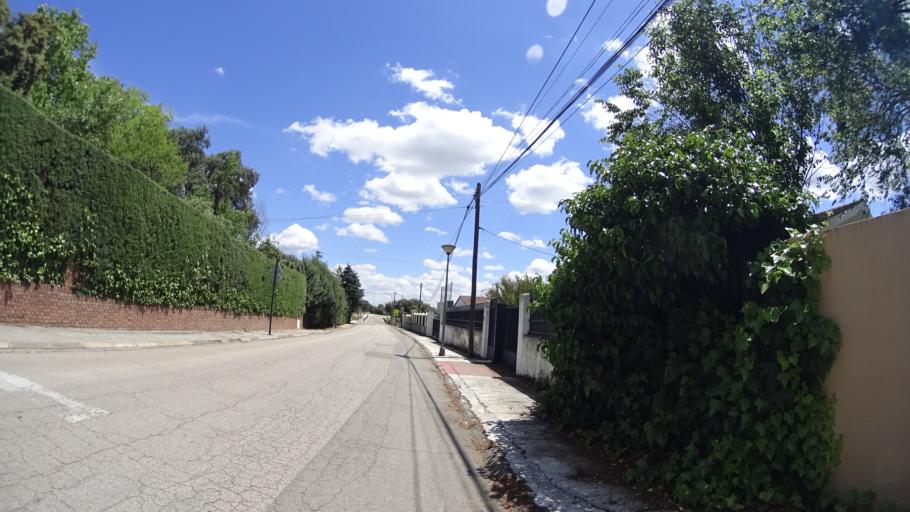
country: ES
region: Madrid
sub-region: Provincia de Madrid
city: Brunete
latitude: 40.4224
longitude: -3.9711
